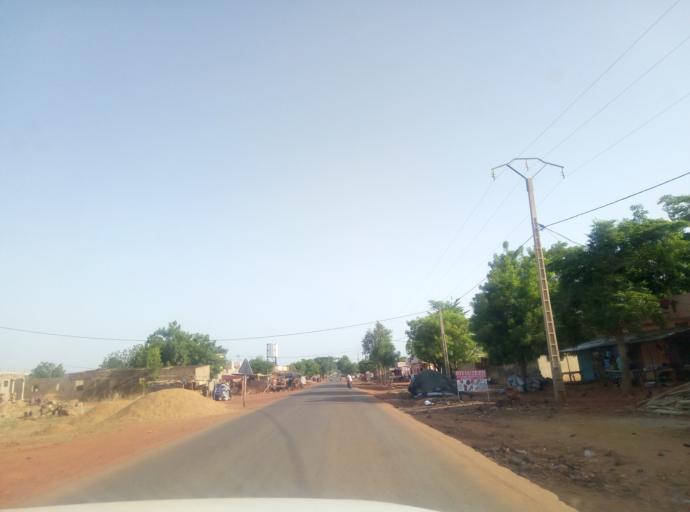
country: ML
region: Bamako
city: Bamako
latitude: 12.5952
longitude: -7.7666
